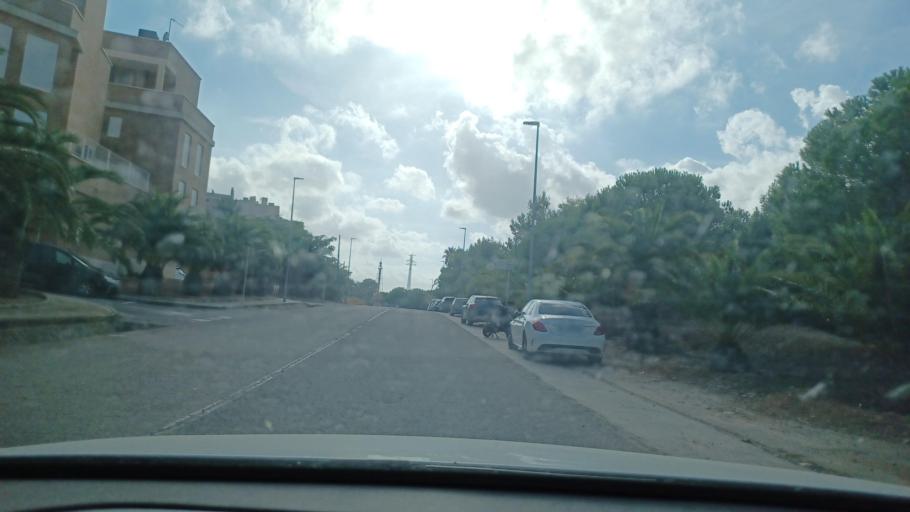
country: ES
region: Catalonia
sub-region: Provincia de Tarragona
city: L'Ampolla
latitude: 40.8135
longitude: 0.7071
